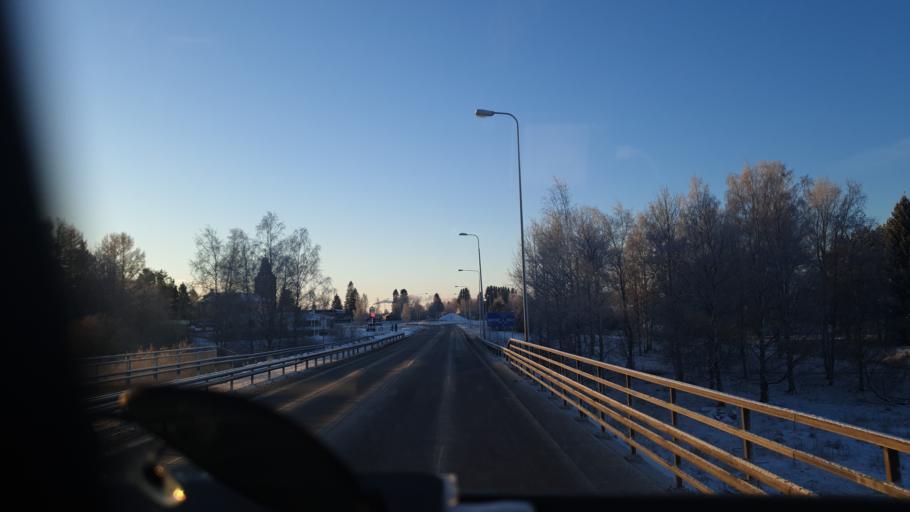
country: FI
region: Northern Ostrobothnia
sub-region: Ylivieska
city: Kalajoki
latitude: 64.2576
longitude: 23.9410
